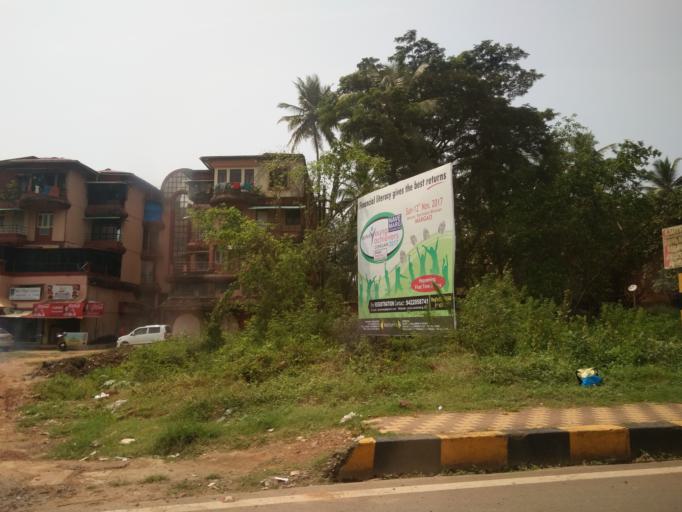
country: IN
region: Goa
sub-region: South Goa
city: Madgaon
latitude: 15.2869
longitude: 73.9554
